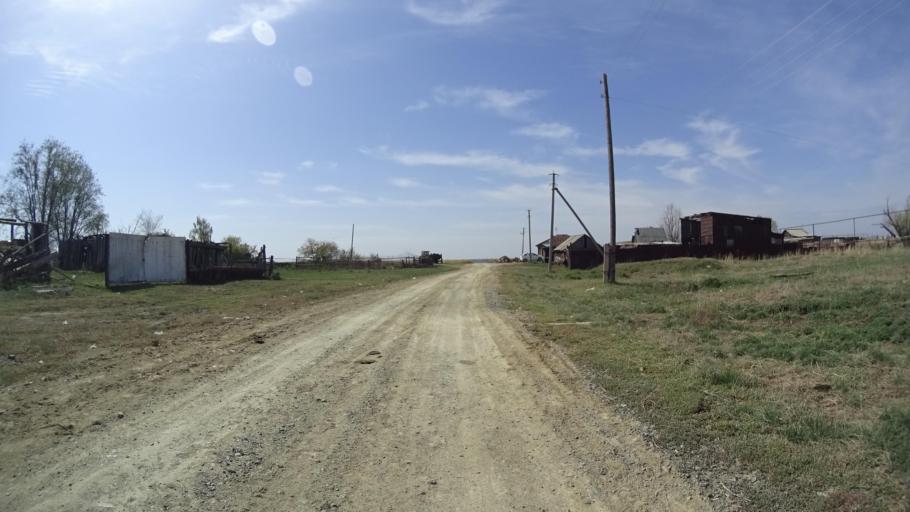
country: RU
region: Chelyabinsk
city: Chesma
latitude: 53.7992
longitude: 61.0176
